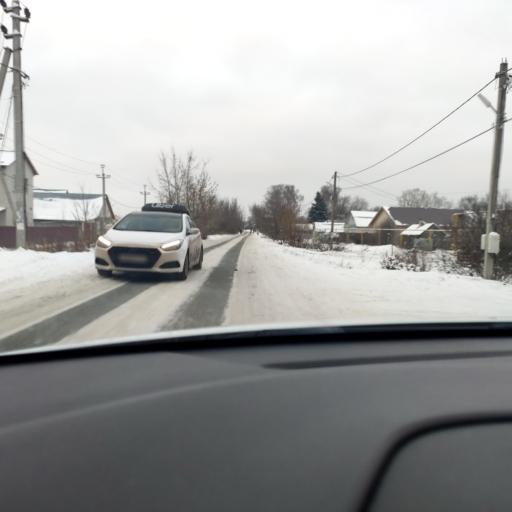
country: RU
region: Tatarstan
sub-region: Gorod Kazan'
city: Kazan
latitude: 55.8734
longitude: 49.1498
